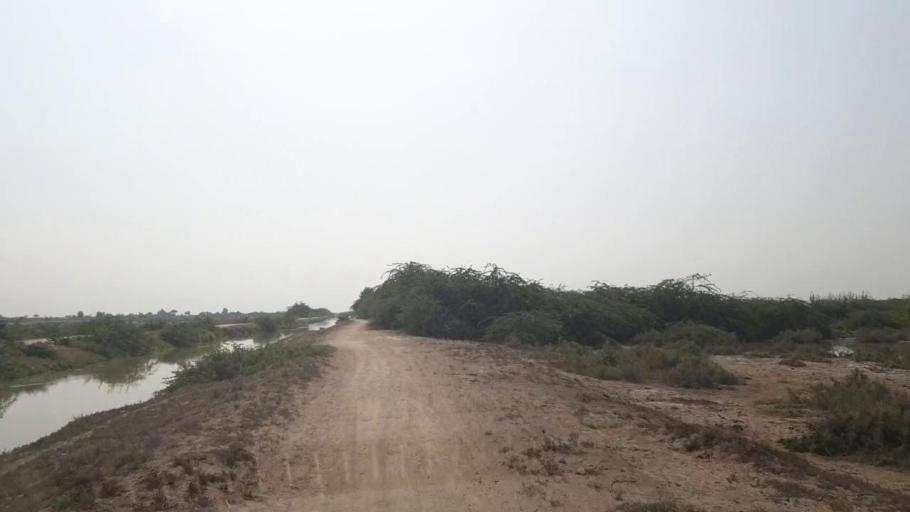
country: PK
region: Sindh
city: Kadhan
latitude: 24.5083
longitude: 68.8503
